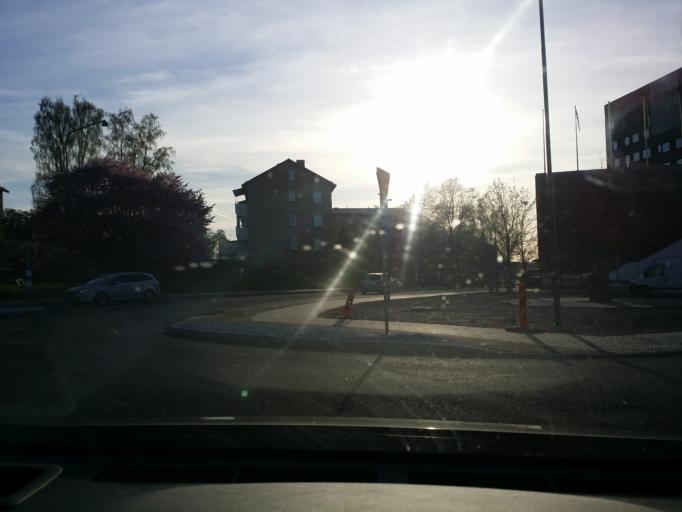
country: SE
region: Dalarna
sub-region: Avesta Kommun
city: Avesta
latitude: 60.1443
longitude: 16.1784
